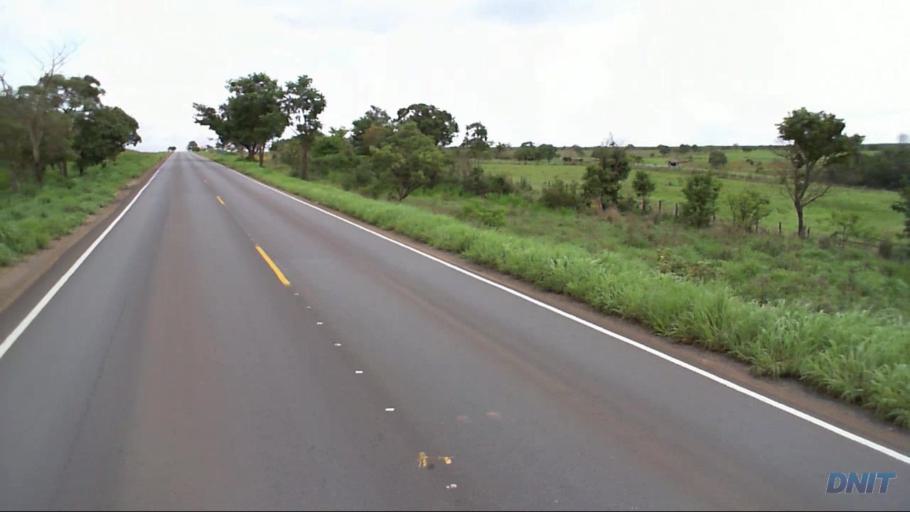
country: BR
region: Goias
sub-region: Padre Bernardo
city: Padre Bernardo
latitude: -15.2864
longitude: -48.2509
